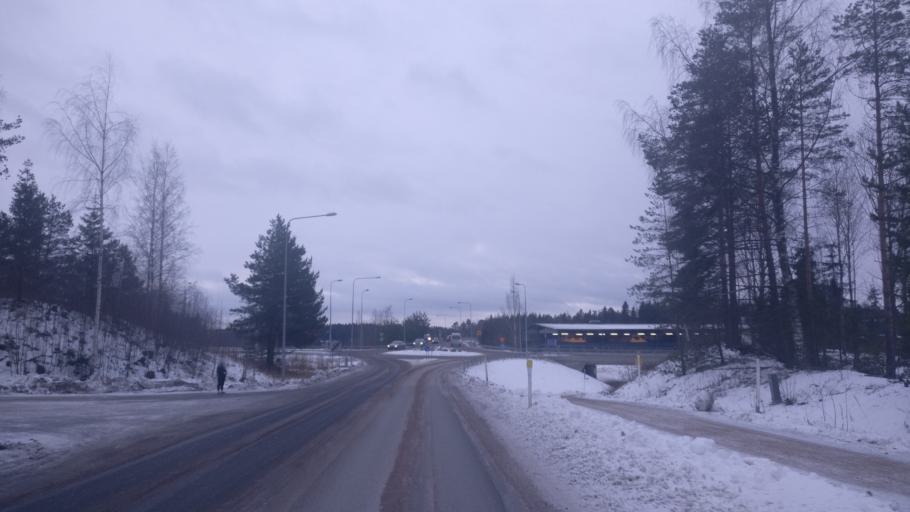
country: FI
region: Paijanne Tavastia
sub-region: Lahti
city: Lahti
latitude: 60.9672
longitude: 25.7239
